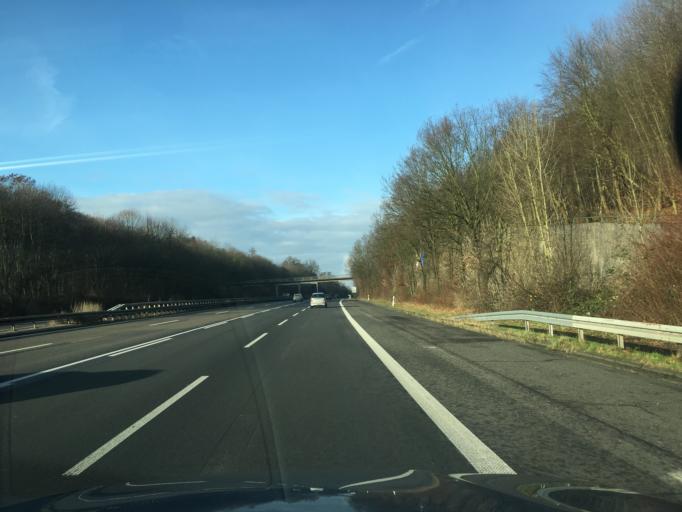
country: DE
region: North Rhine-Westphalia
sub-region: Regierungsbezirk Koln
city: Konigswinter
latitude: 50.7283
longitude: 7.1578
